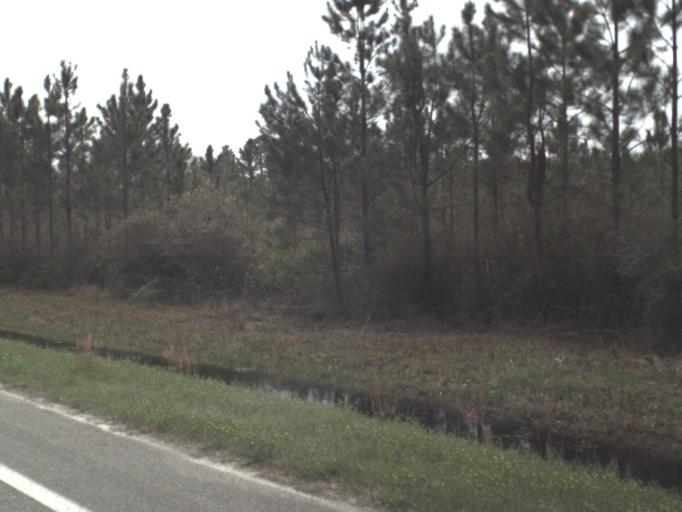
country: US
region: Florida
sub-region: Gulf County
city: Wewahitchka
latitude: 30.0495
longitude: -85.1871
